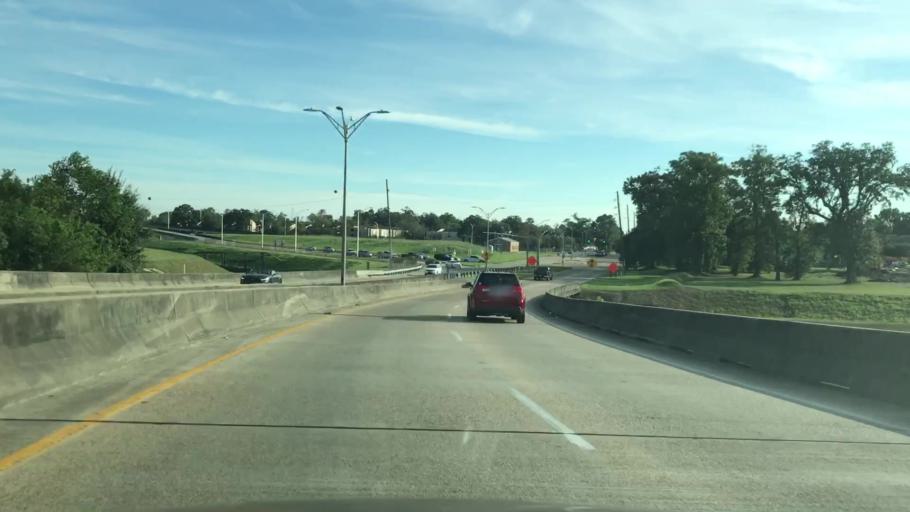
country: US
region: Louisiana
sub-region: Jefferson Parish
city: River Ridge
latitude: 29.9721
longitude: -90.2048
